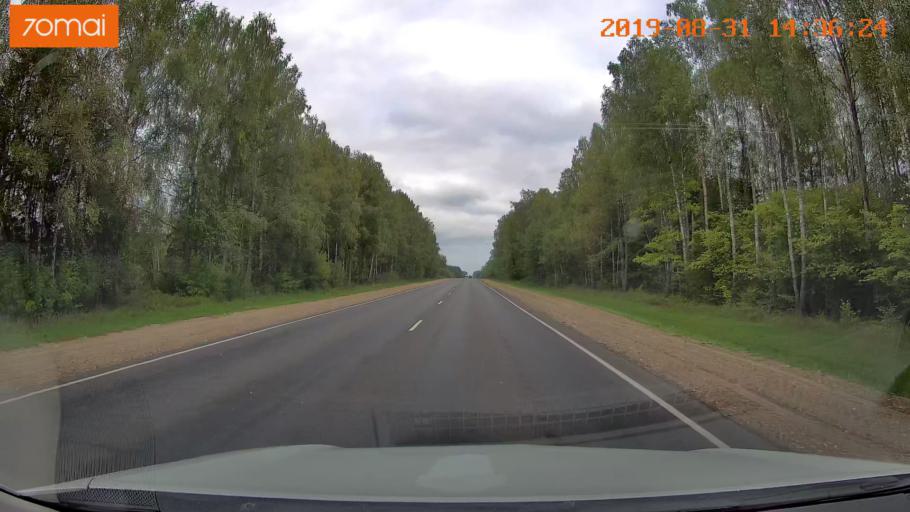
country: RU
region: Smolensk
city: Yekimovichi
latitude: 54.1697
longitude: 33.4788
